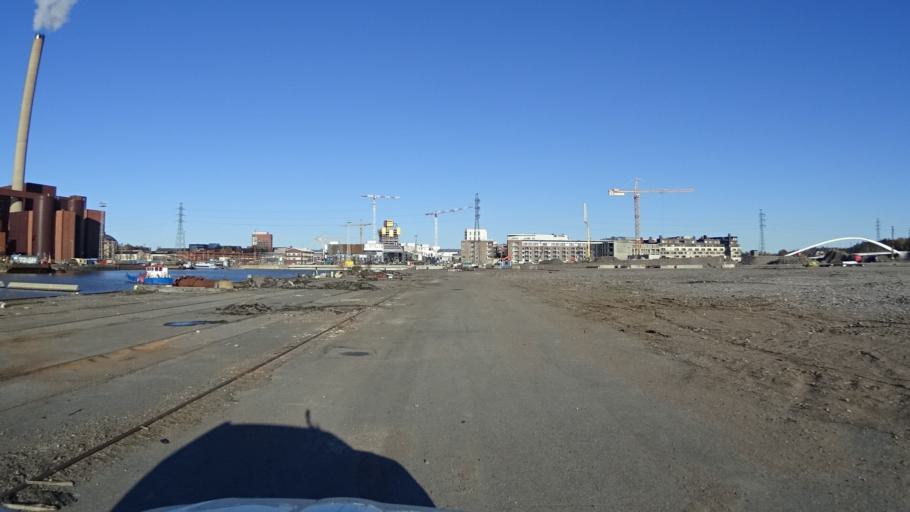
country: FI
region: Uusimaa
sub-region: Helsinki
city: Helsinki
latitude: 60.1803
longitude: 24.9734
